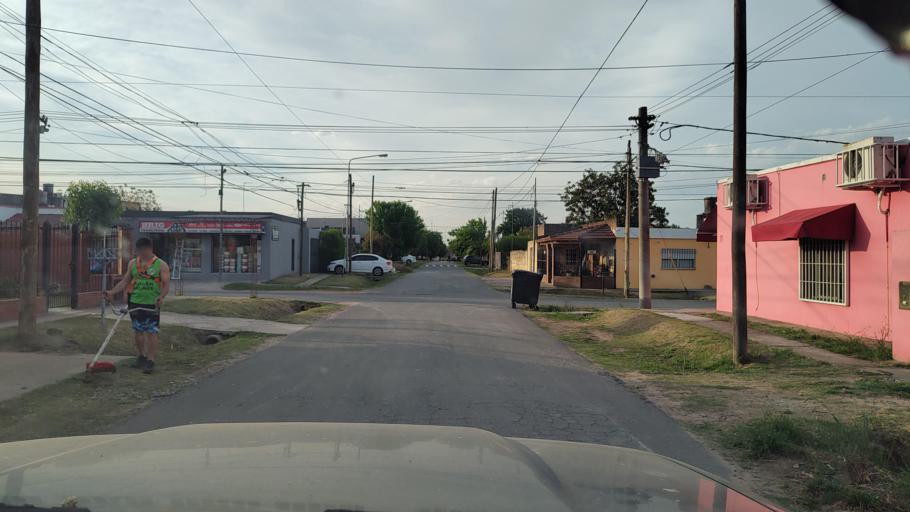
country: AR
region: Buenos Aires
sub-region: Partido de Lujan
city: Lujan
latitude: -34.5697
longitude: -59.1351
